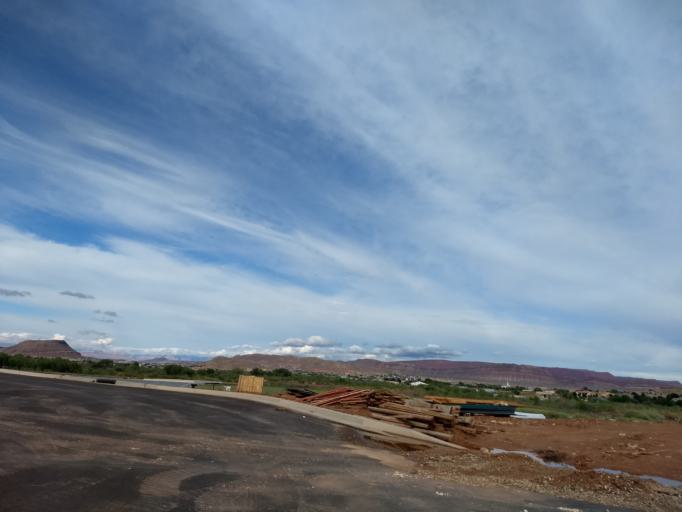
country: US
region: Utah
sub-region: Washington County
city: Saint George
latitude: 37.0893
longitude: -113.5415
